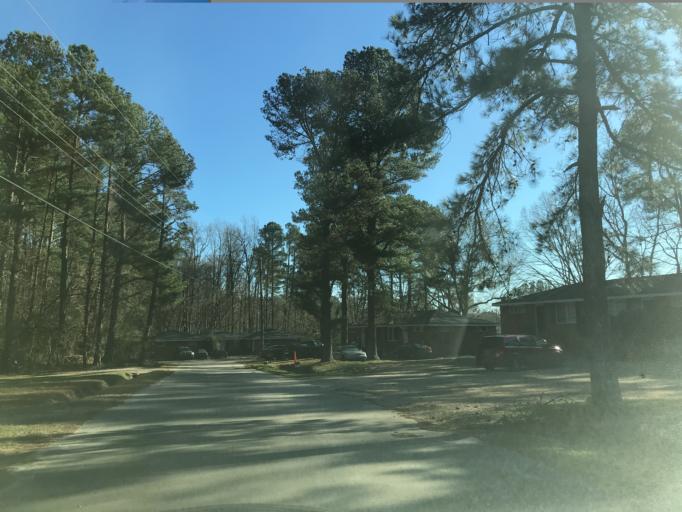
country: US
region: North Carolina
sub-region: Wake County
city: Raleigh
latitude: 35.8409
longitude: -78.6071
